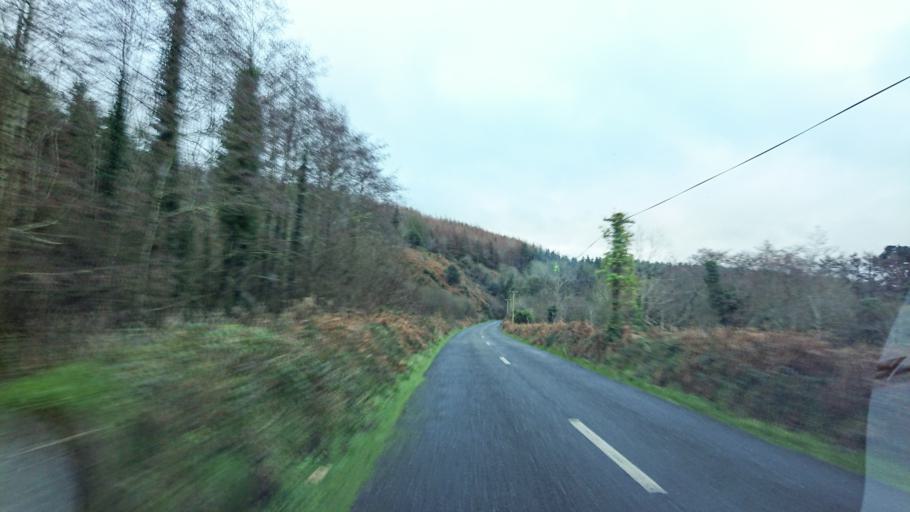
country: IE
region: Munster
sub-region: Waterford
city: Portlaw
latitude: 52.2144
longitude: -7.4192
